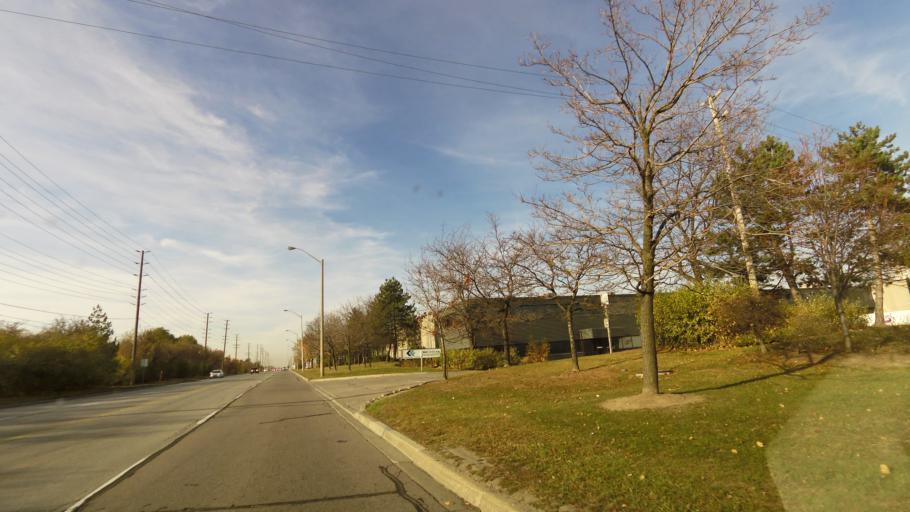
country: CA
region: Ontario
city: Brampton
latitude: 43.7299
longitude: -79.7008
